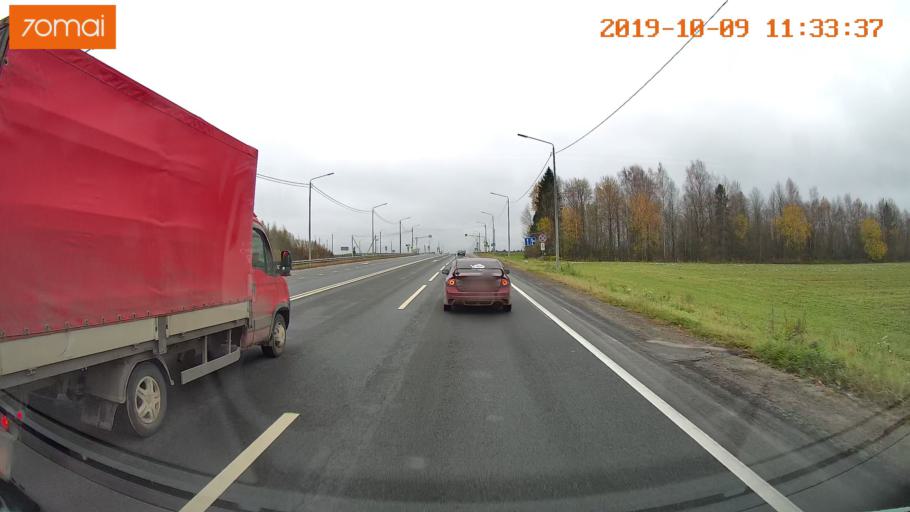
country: RU
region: Vologda
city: Gryazovets
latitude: 59.0231
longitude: 40.1147
